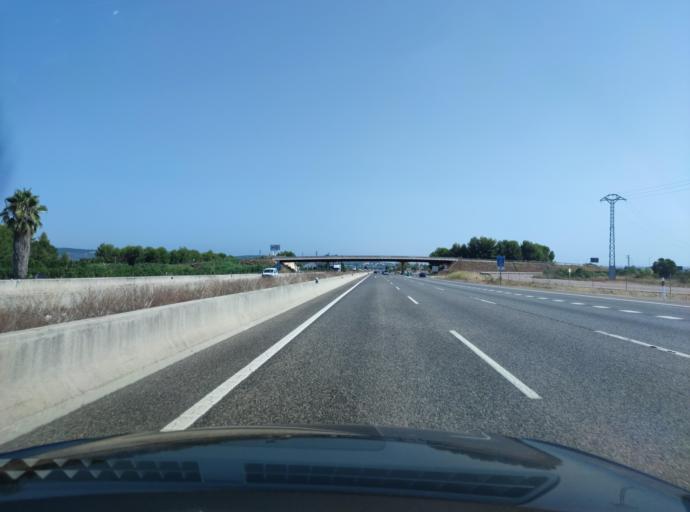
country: ES
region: Valencia
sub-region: Provincia de Valencia
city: Beneixida
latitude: 39.0564
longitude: -0.5444
